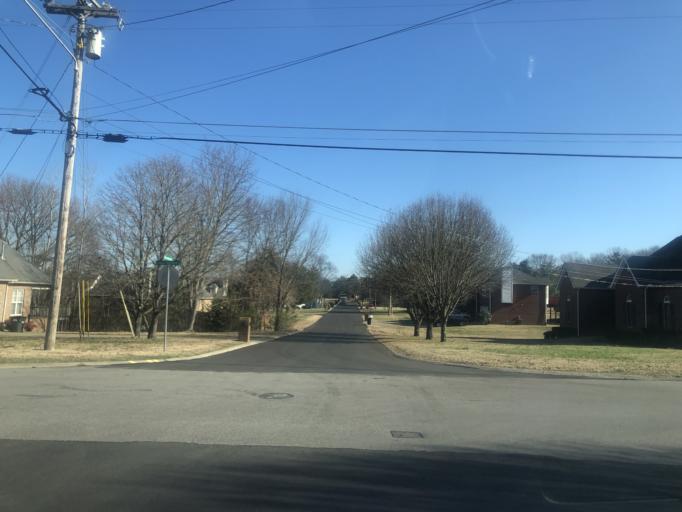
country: US
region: Tennessee
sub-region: Rutherford County
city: Smyrna
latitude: 35.9732
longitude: -86.5399
